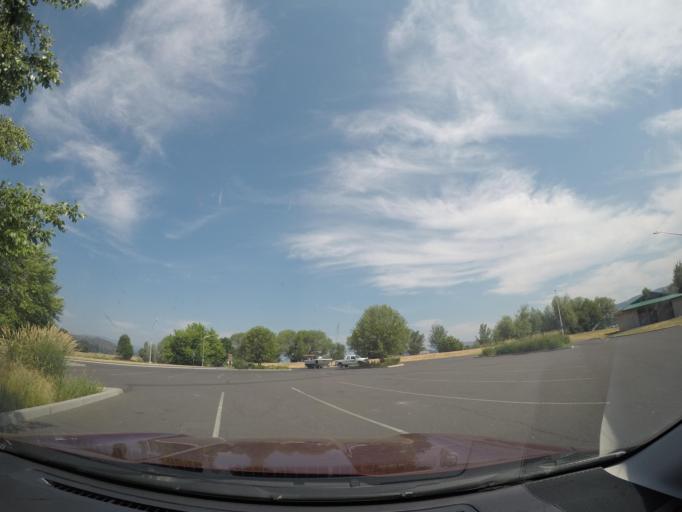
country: US
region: Oregon
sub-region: Klamath County
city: Klamath Falls
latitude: 42.2341
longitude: -121.8140
